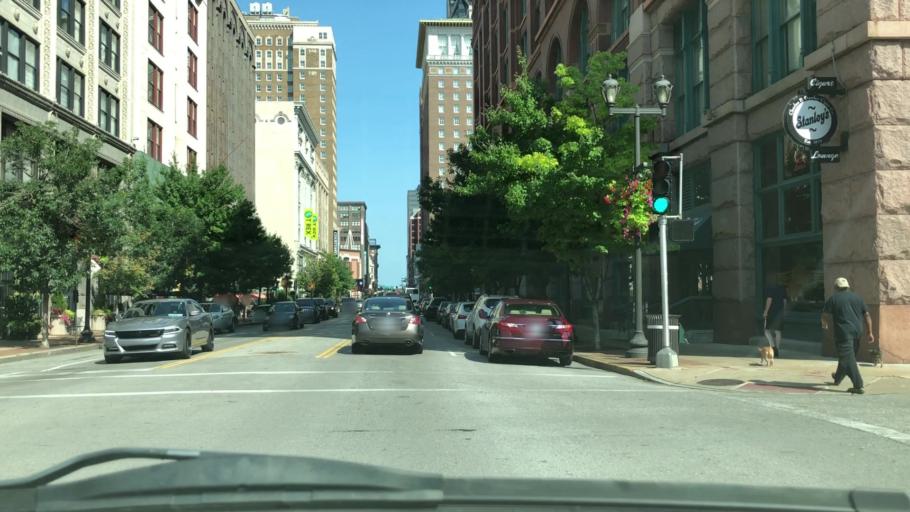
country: US
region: Missouri
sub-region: City of Saint Louis
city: St. Louis
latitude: 38.6314
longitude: -90.1951
